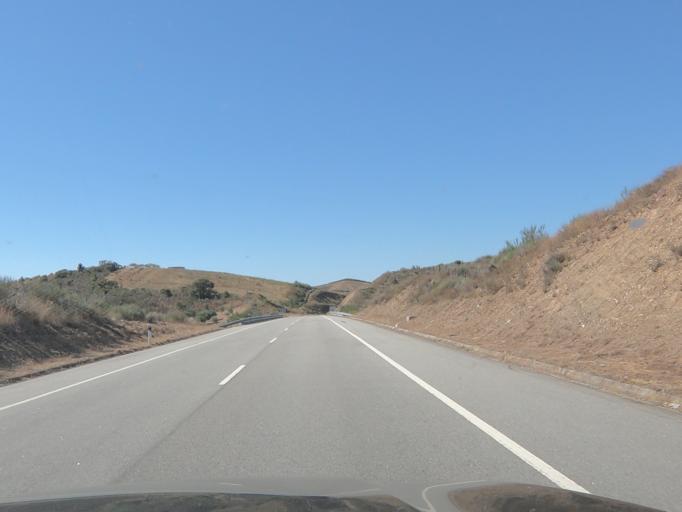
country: PT
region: Braganca
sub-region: Mirandela
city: Mirandela
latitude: 41.5190
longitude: -7.2339
